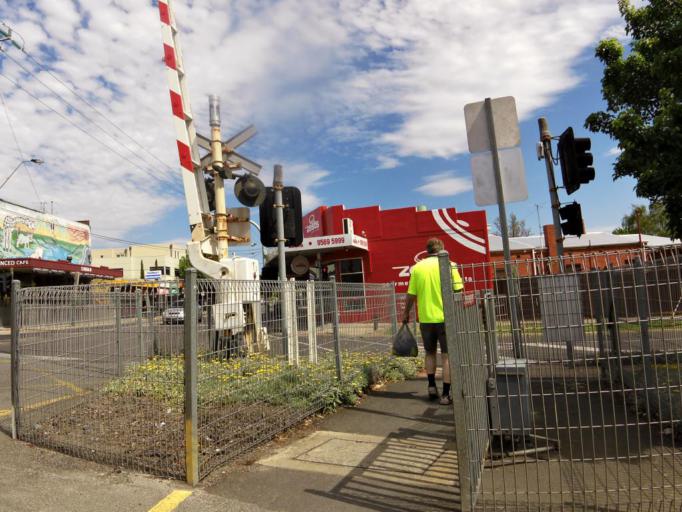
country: AU
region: Victoria
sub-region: Glen Eira
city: Murrumbeena
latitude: -37.8944
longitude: 145.0767
